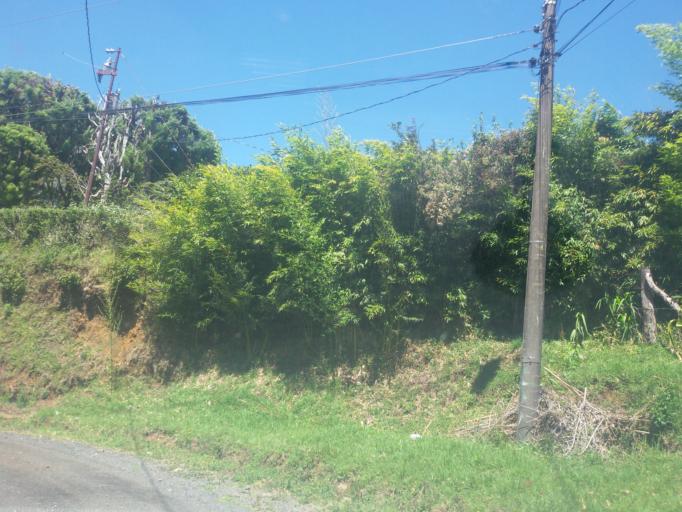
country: CR
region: Heredia
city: Santo Domingo
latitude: 10.0790
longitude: -84.0952
